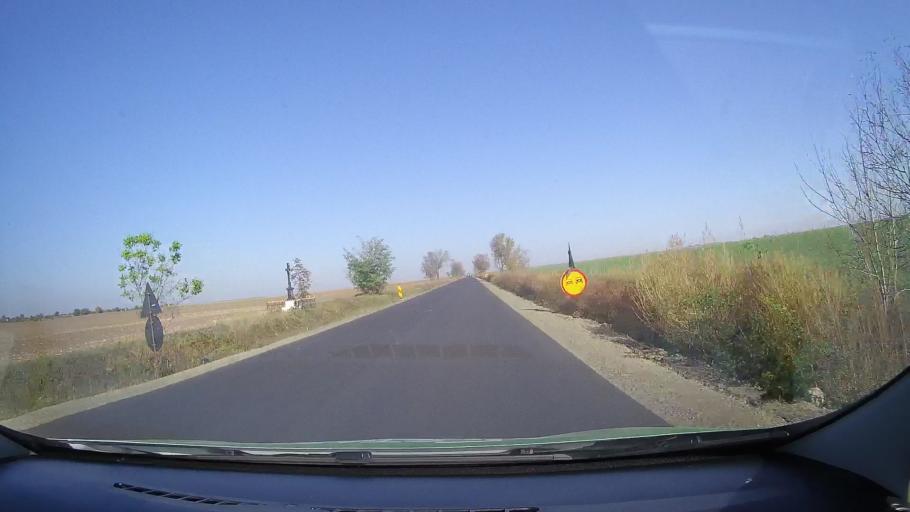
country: RO
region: Satu Mare
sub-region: Comuna Tiream
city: Tiream
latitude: 47.6246
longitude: 22.4679
